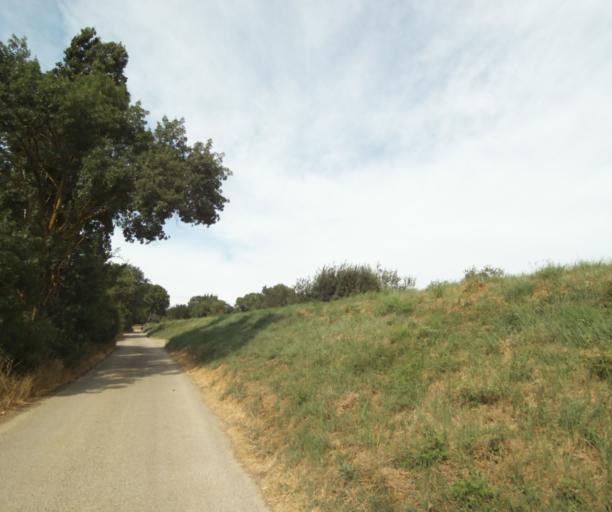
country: FR
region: Languedoc-Roussillon
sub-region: Departement de l'Herault
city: Marsillargues
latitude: 43.6376
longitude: 4.1888
